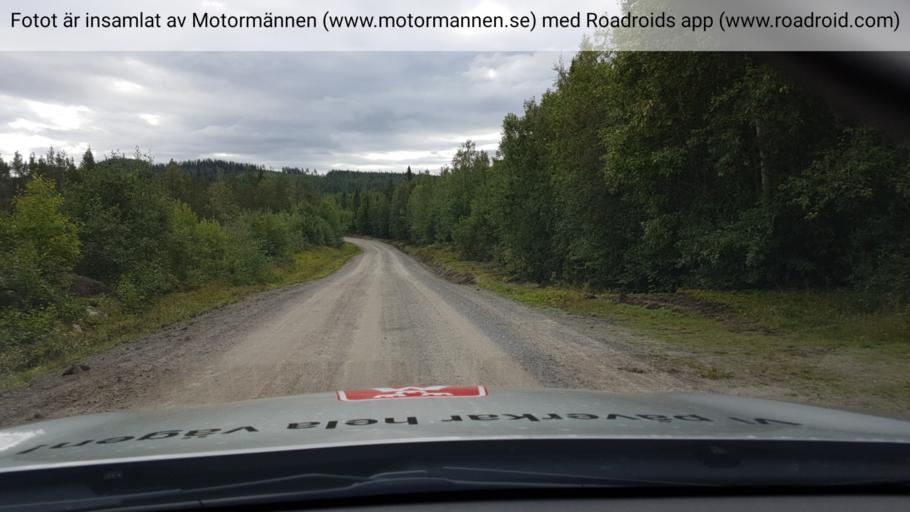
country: SE
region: Jaemtland
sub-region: Ragunda Kommun
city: Hammarstrand
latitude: 62.9283
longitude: 16.1259
